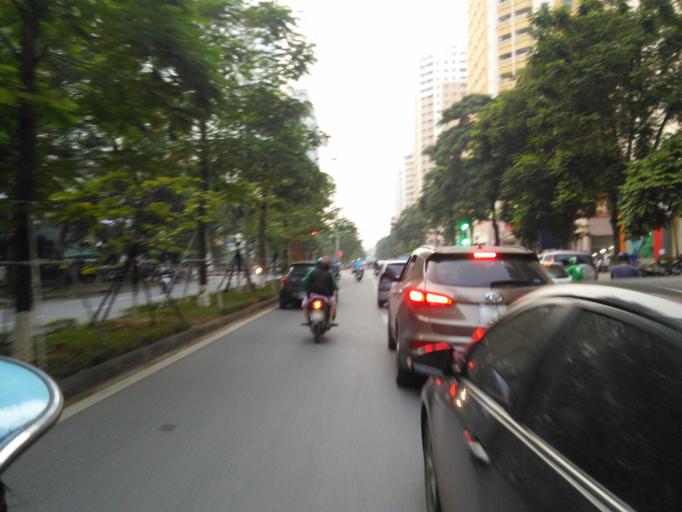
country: VN
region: Ha Noi
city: Thanh Xuan
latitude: 21.0067
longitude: 105.8035
